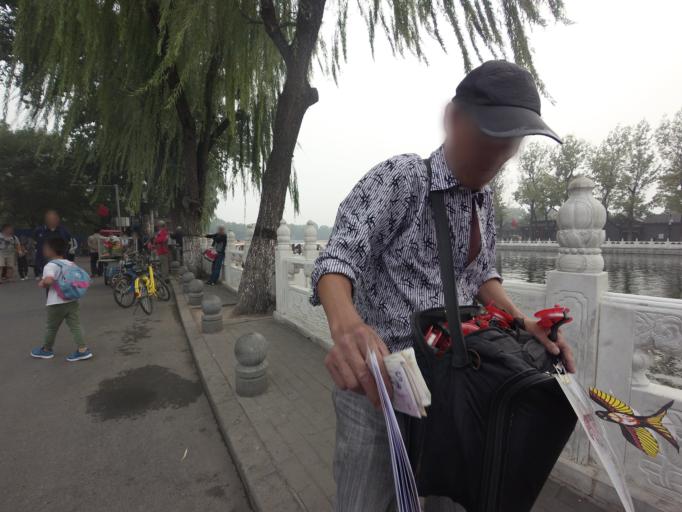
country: CN
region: Beijing
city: Jingshan
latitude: 39.9371
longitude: 116.3884
